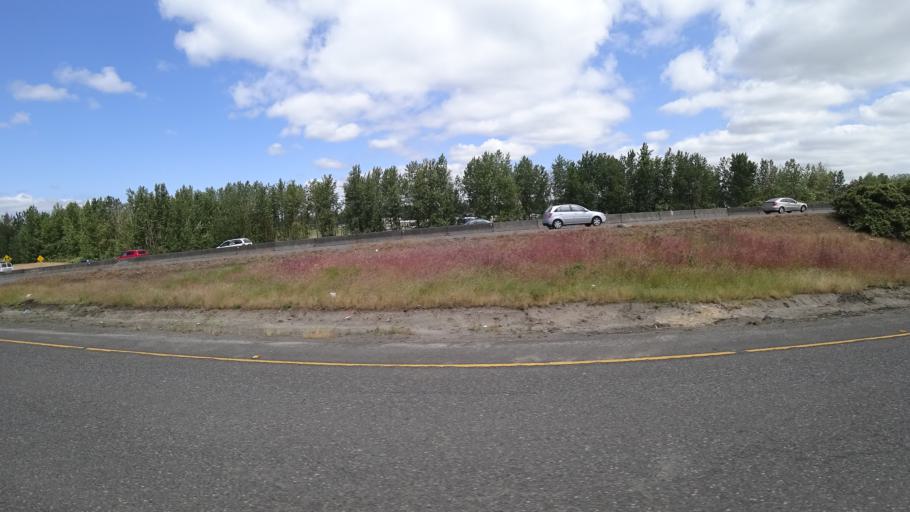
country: US
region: Washington
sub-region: Clark County
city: Vancouver
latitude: 45.6182
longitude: -122.6554
